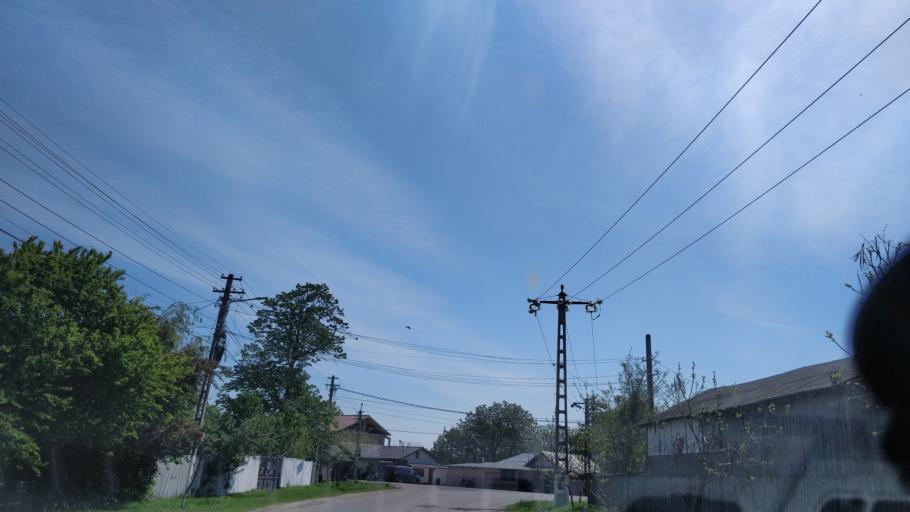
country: RO
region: Vrancea
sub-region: Comuna Suraia
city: Suraia
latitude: 45.6703
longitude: 27.3863
